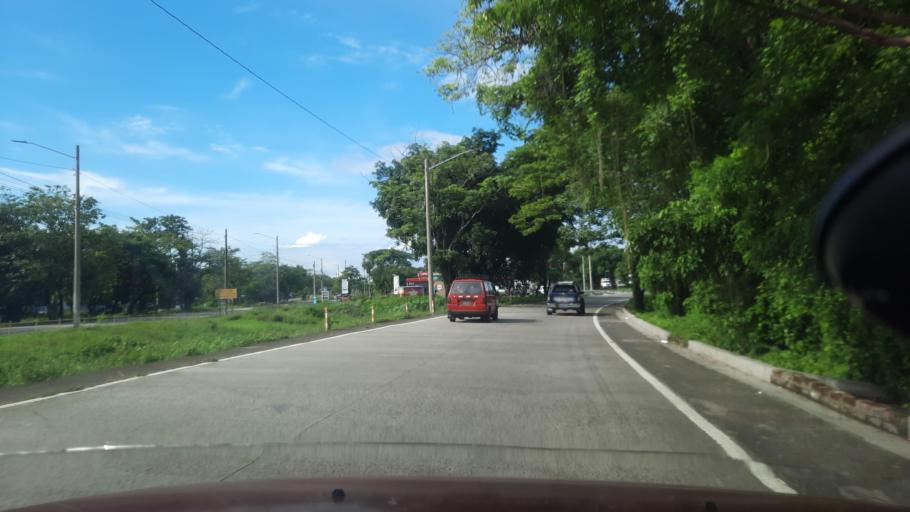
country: SV
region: La Paz
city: El Rosario
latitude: 13.4838
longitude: -89.0665
